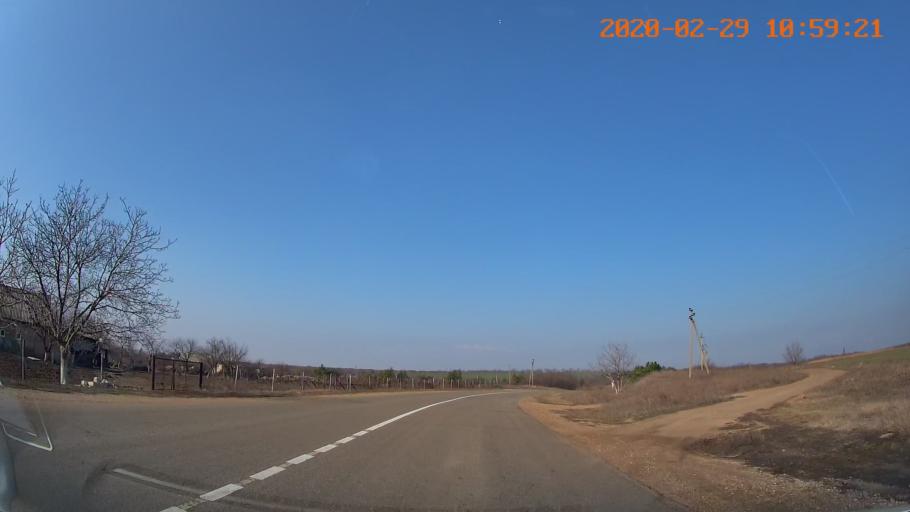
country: MD
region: Telenesti
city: Grigoriopol
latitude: 47.1646
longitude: 29.2932
